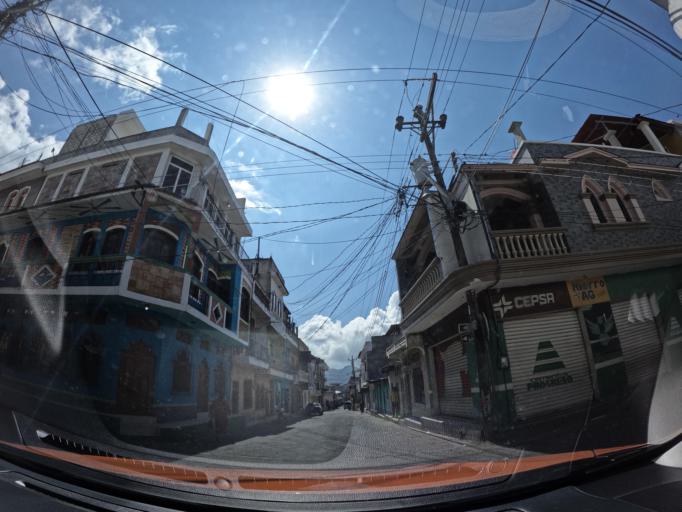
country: GT
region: Solola
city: Santiago Atitlan
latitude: 14.6374
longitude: -91.2313
